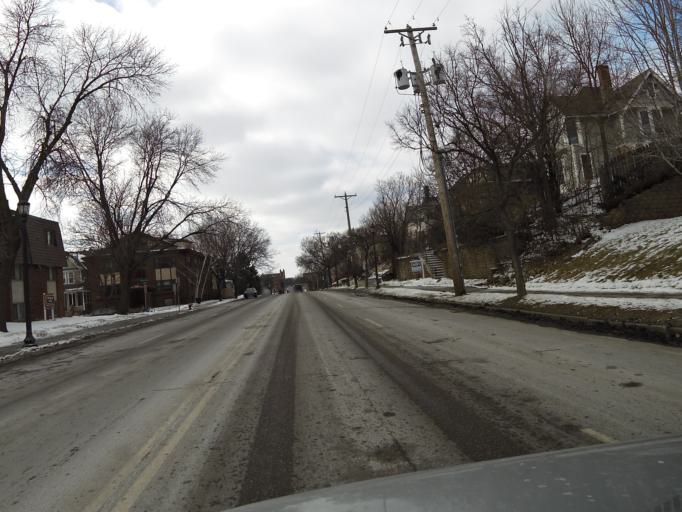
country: US
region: Minnesota
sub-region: Hennepin County
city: Minneapolis
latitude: 44.9627
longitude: -93.2835
